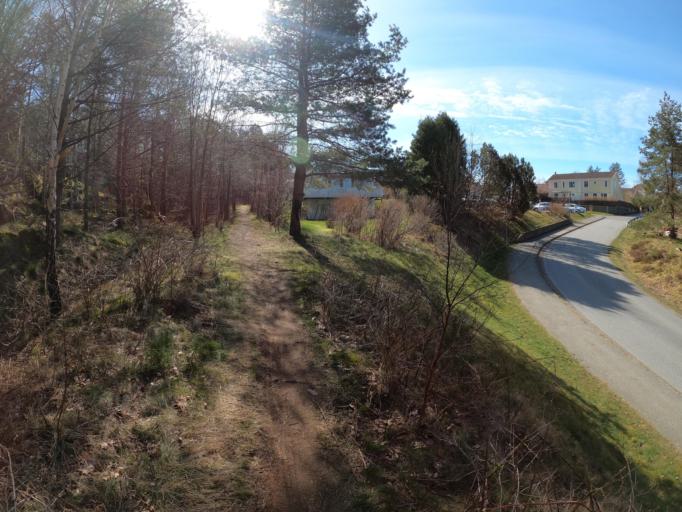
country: SE
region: Vaestra Goetaland
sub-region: Harryda Kommun
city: Molnlycke
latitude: 57.6457
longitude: 12.1124
